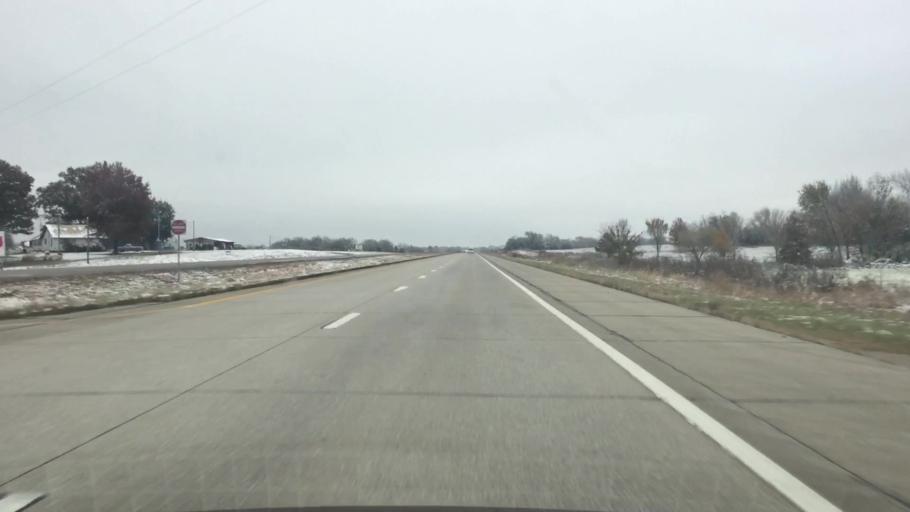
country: US
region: Missouri
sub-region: Saint Clair County
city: Osceola
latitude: 38.1843
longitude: -93.7330
